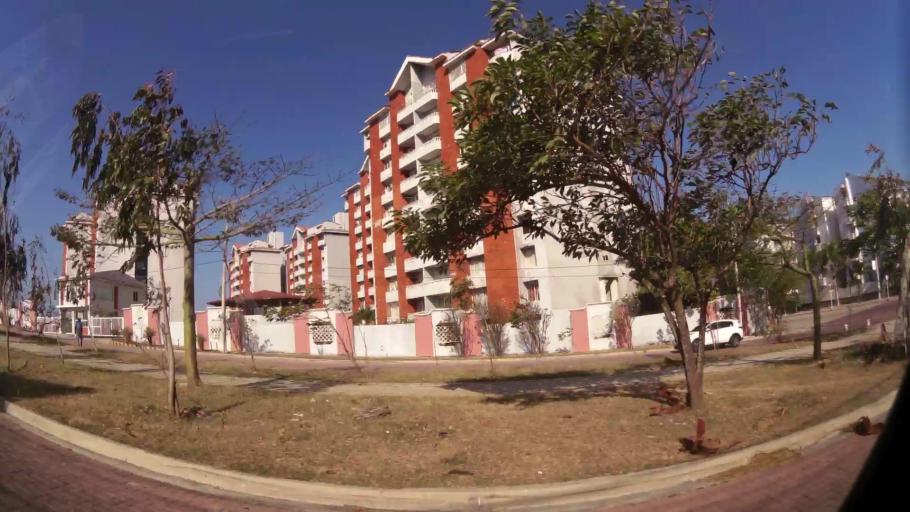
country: CO
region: Atlantico
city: Barranquilla
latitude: 11.0028
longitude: -74.8332
